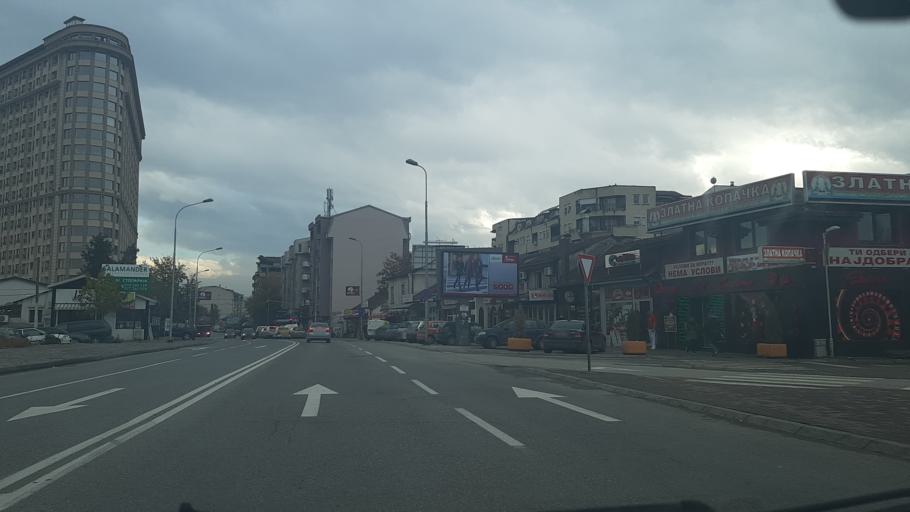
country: MK
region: Karpos
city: Skopje
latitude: 41.9867
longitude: 21.4372
